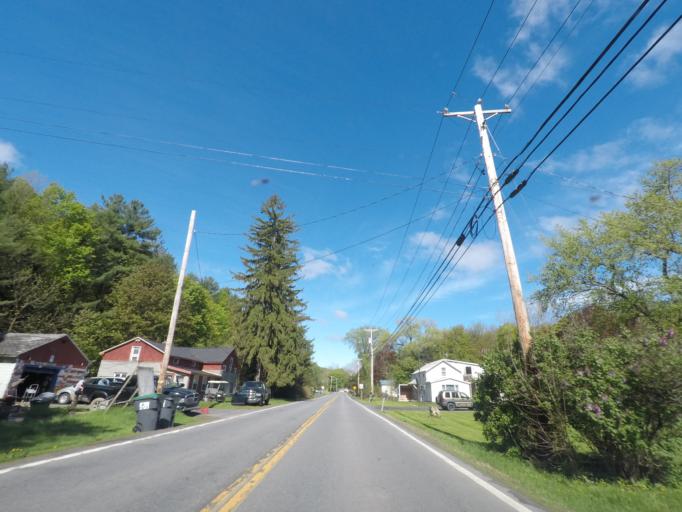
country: US
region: New York
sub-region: Albany County
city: Ravena
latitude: 42.4685
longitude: -73.8856
